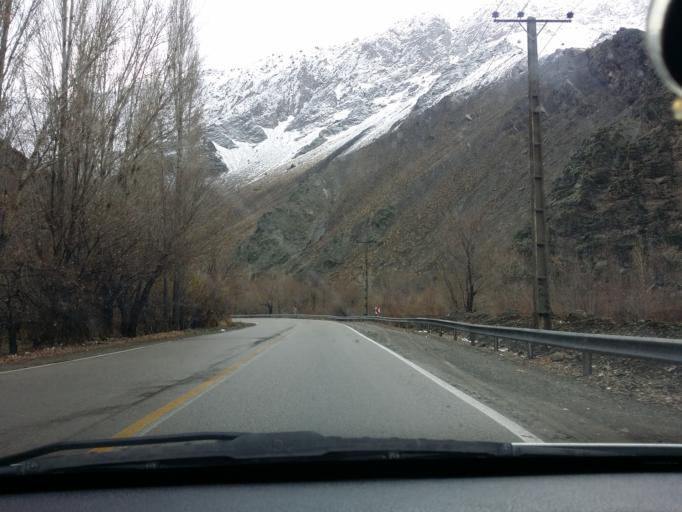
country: IR
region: Tehran
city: Tajrish
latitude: 36.0177
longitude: 51.2789
